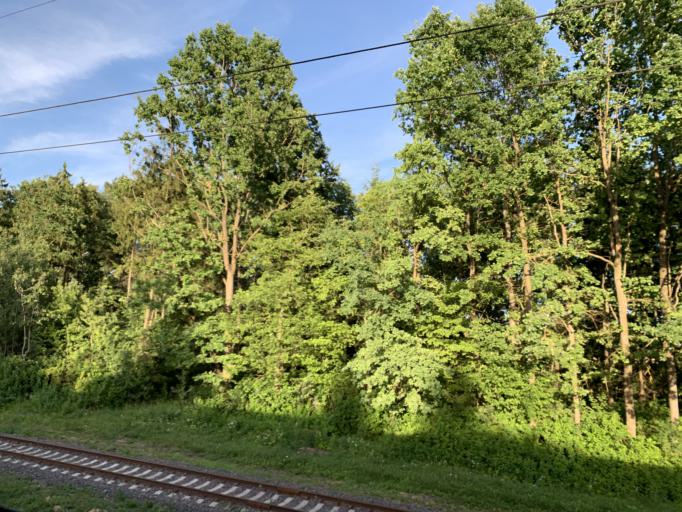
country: BY
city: Fanipol
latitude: 53.7569
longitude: 27.3609
